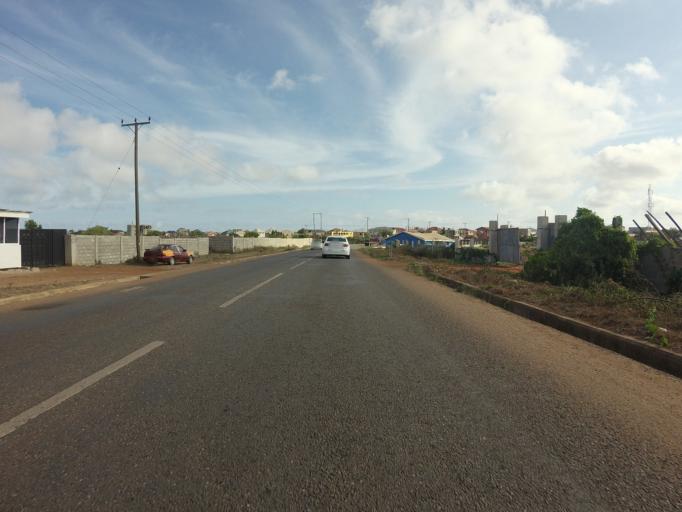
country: GH
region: Greater Accra
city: Teshi Old Town
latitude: 5.5905
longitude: -0.1362
